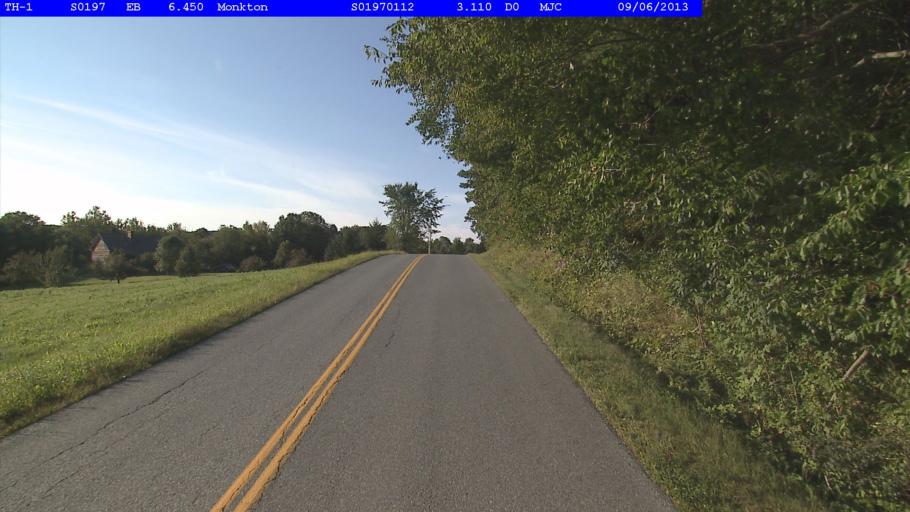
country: US
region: Vermont
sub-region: Chittenden County
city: Hinesburg
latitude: 44.2221
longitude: -73.1526
